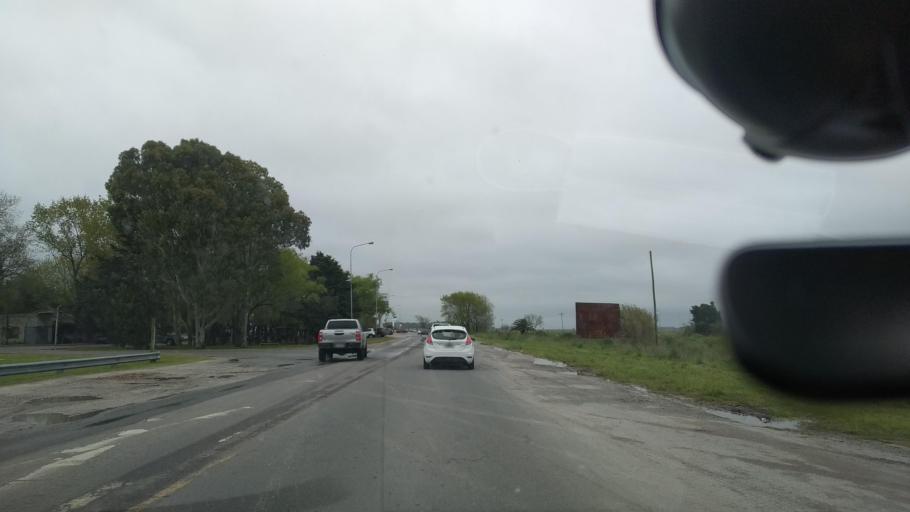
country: AR
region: Buenos Aires
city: Veronica
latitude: -35.5323
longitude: -57.3220
